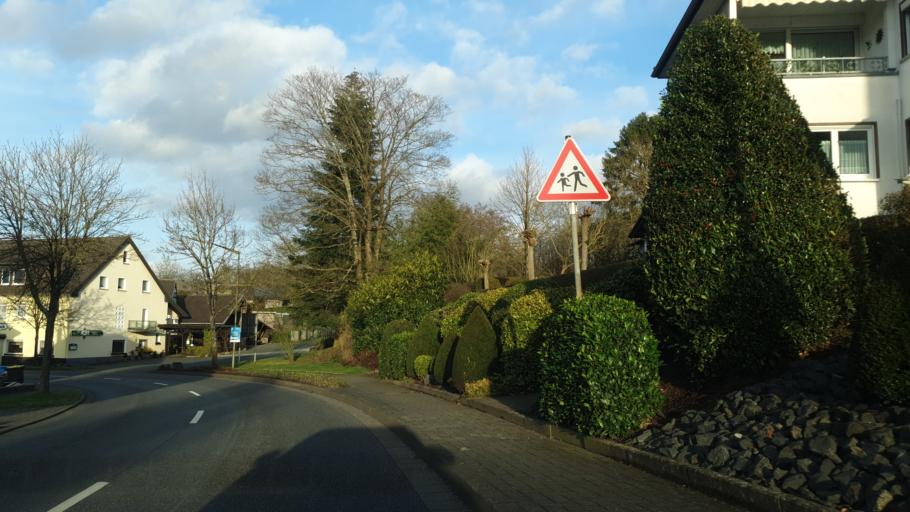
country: DE
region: Rheinland-Pfalz
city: Fluterschen
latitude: 50.6640
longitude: 7.6262
